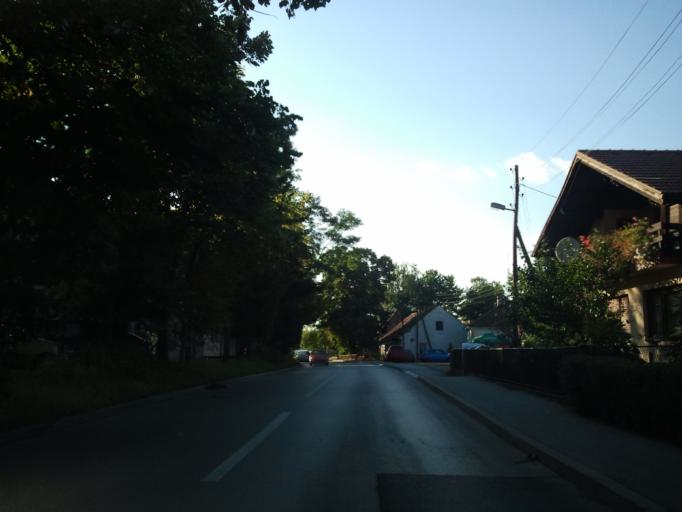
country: HR
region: Sisacko-Moslavacka
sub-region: Grad Sisak
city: Sisak
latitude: 45.4578
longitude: 16.3916
